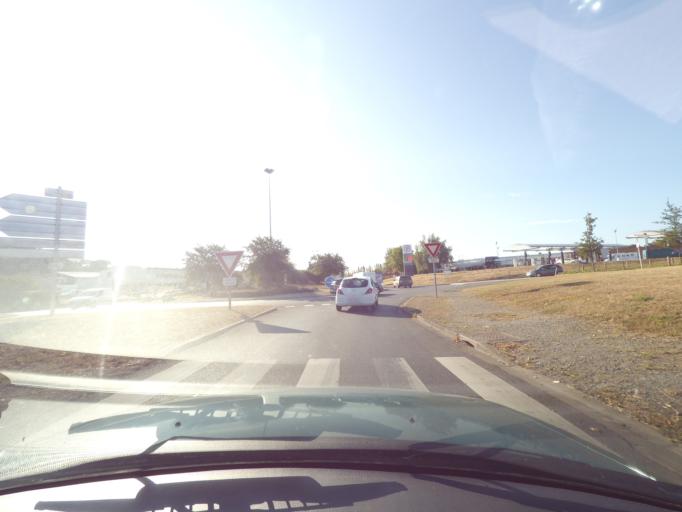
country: FR
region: Poitou-Charentes
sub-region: Departement des Deux-Sevres
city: Chatillon-sur-Thouet
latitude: 46.6501
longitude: -0.2232
